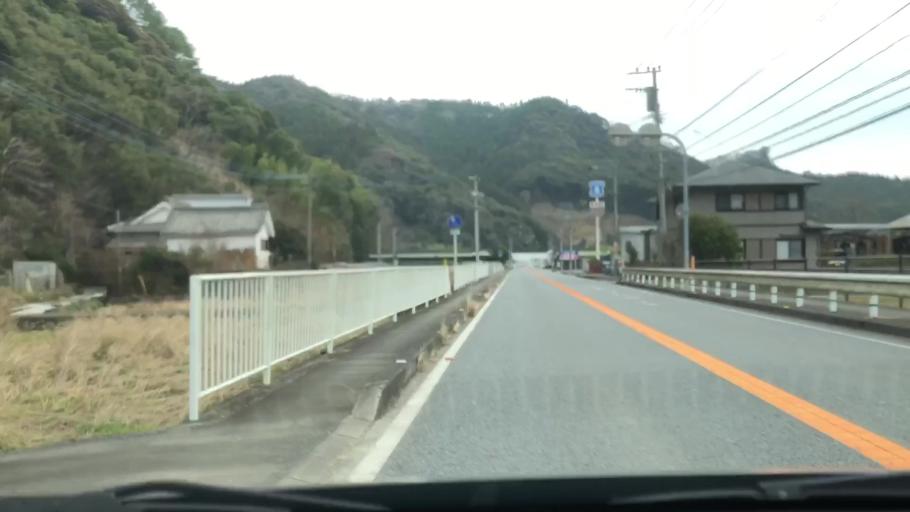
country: JP
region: Oita
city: Saiki
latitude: 32.9858
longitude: 131.8418
